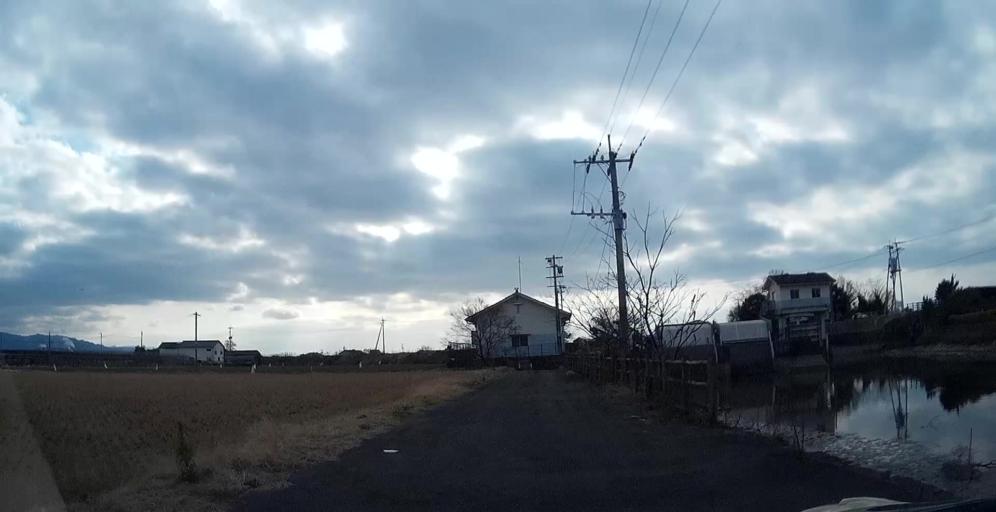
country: JP
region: Kumamoto
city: Yatsushiro
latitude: 32.5525
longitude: 130.6233
